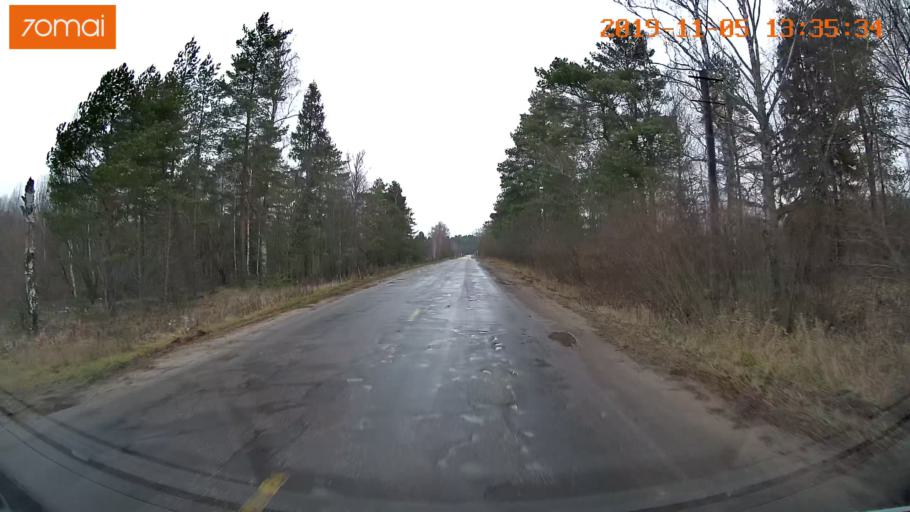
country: RU
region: Ivanovo
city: Shuya
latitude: 56.9087
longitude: 41.3867
